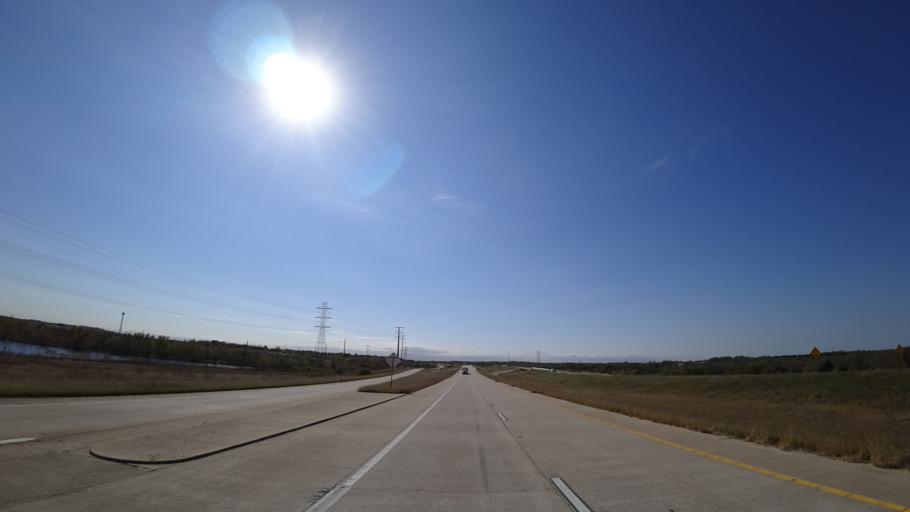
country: US
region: Texas
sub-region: Travis County
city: Garfield
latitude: 30.1450
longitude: -97.6614
